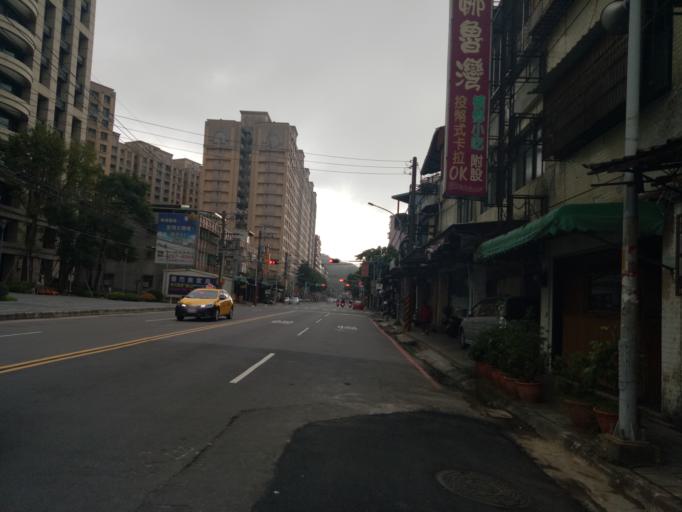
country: TW
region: Taipei
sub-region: Taipei
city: Banqiao
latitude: 24.9550
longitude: 121.4131
